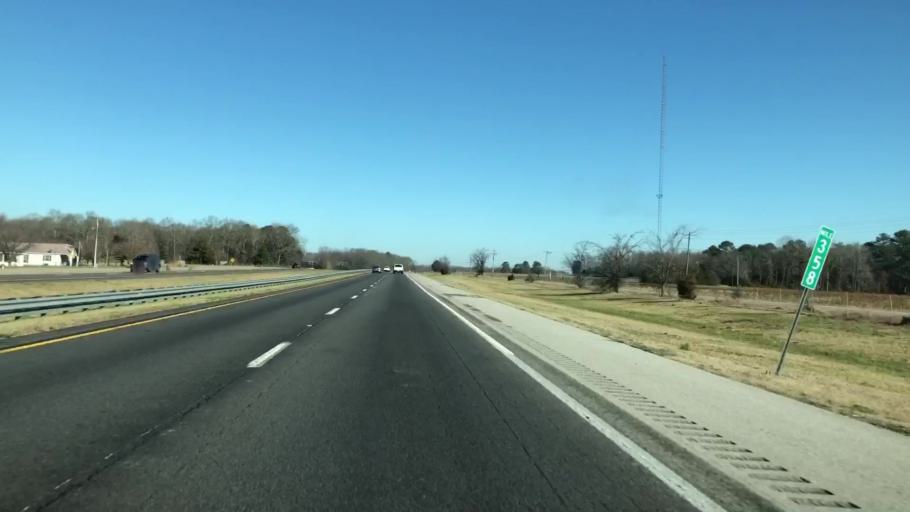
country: US
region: Alabama
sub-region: Limestone County
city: Athens
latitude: 34.8816
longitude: -86.9190
